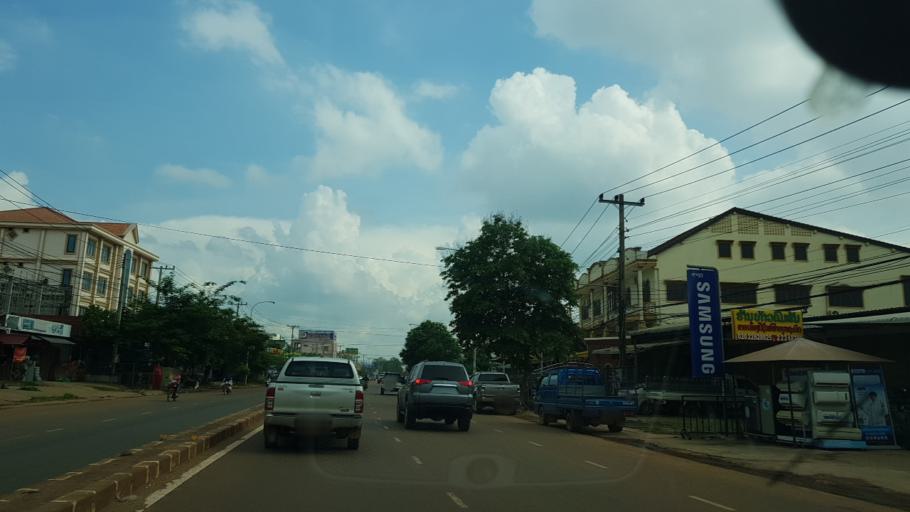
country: LA
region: Vientiane
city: Vientiane
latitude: 18.0237
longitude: 102.6516
